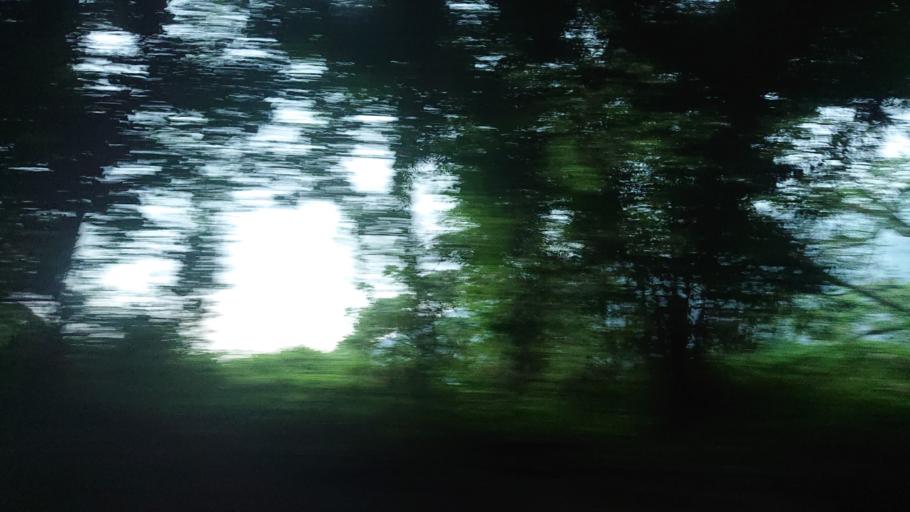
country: TW
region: Taiwan
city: Lugu
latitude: 23.5918
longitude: 120.7238
